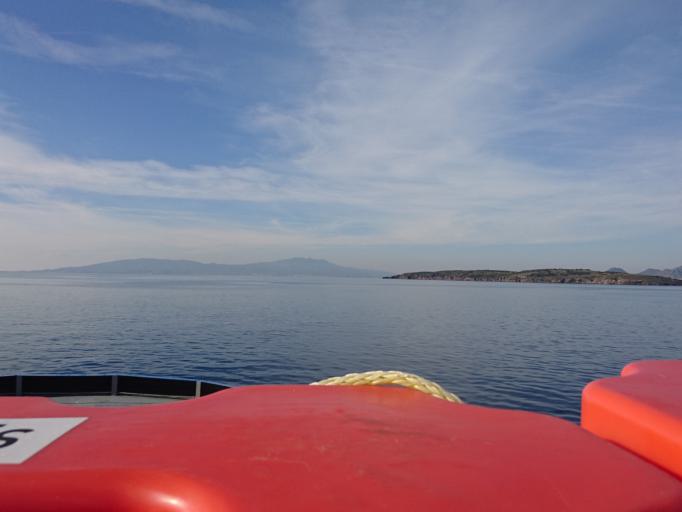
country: TR
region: Mugla
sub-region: Bodrum
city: Bodrum
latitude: 37.0060
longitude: 27.4078
